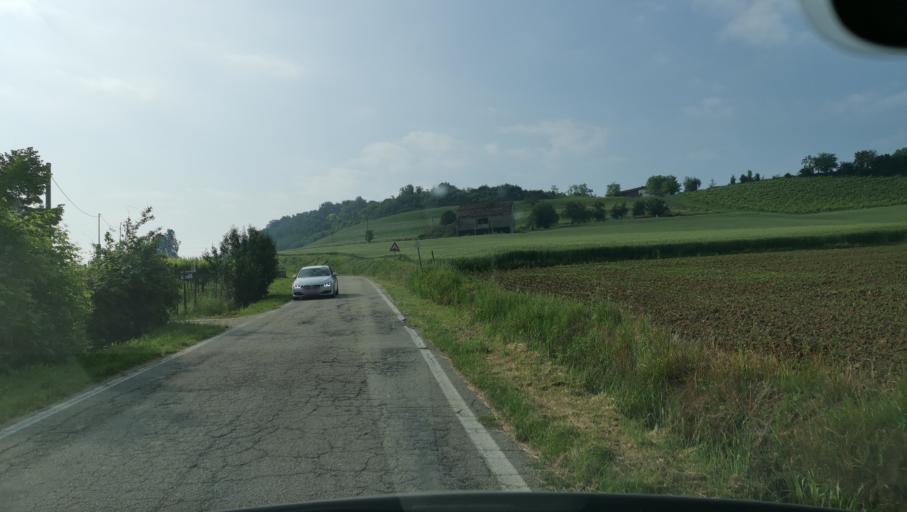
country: IT
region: Piedmont
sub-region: Provincia di Alessandria
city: Castelletto Merli
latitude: 45.0605
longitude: 8.2430
